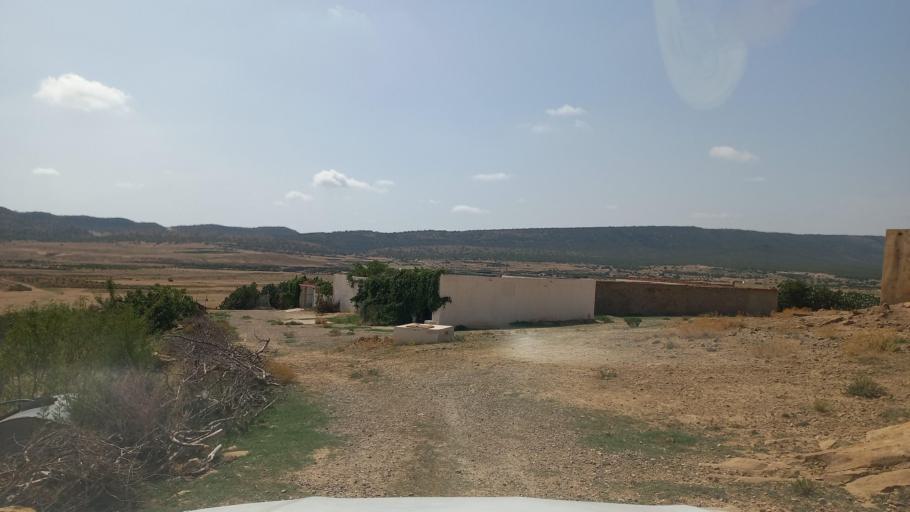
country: TN
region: Al Qasrayn
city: Sbiba
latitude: 35.3975
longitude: 8.9624
